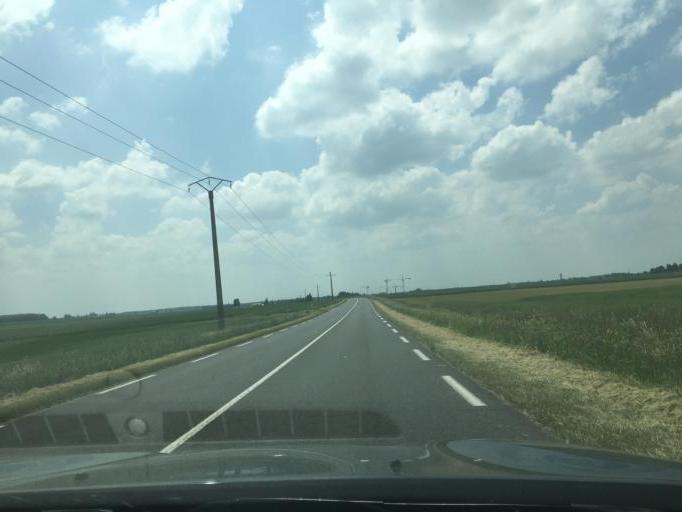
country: FR
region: Centre
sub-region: Departement du Loiret
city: Rebrechien
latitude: 47.9794
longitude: 2.0585
